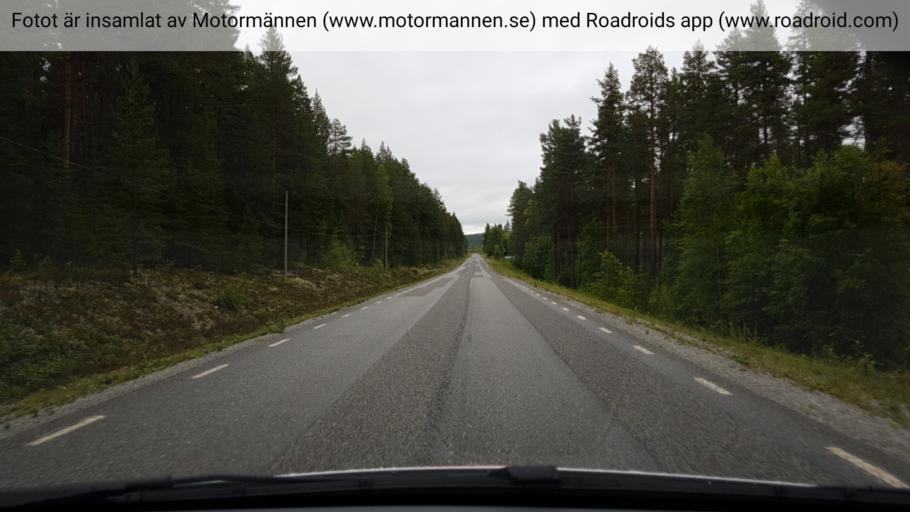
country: SE
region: Vaesterbotten
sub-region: Dorotea Kommun
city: Dorotea
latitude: 63.8373
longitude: 16.1092
